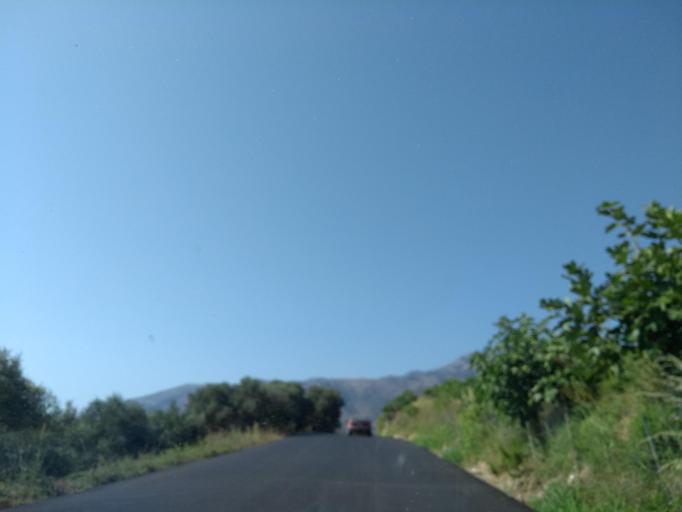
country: GR
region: Crete
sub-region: Nomos Chanias
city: Georgioupolis
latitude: 35.3321
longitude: 24.3015
